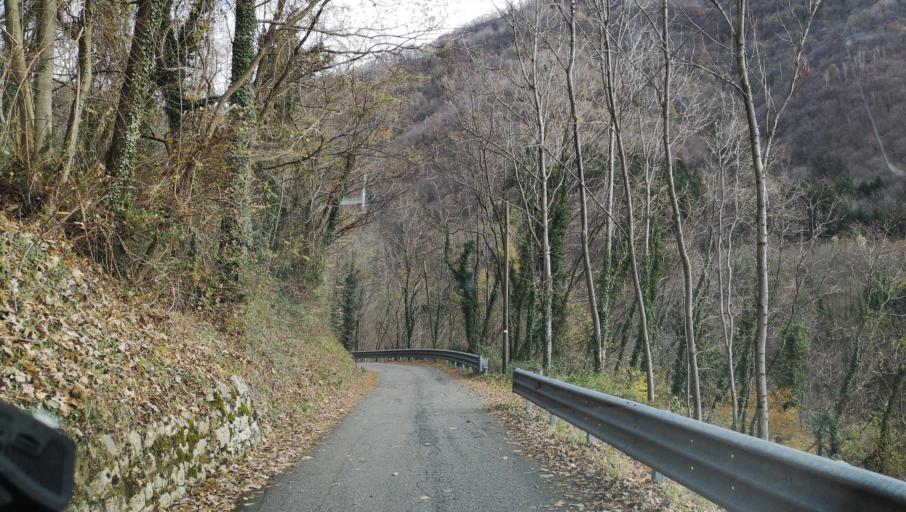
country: IT
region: Friuli Venezia Giulia
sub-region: Provincia di Udine
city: Attimis
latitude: 46.2187
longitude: 13.3218
